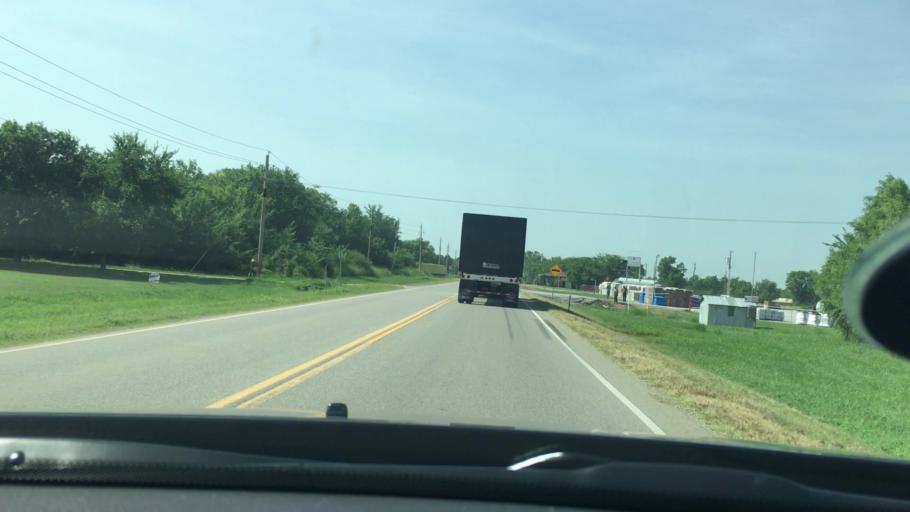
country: US
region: Oklahoma
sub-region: Coal County
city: Coalgate
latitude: 34.4737
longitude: -96.2178
